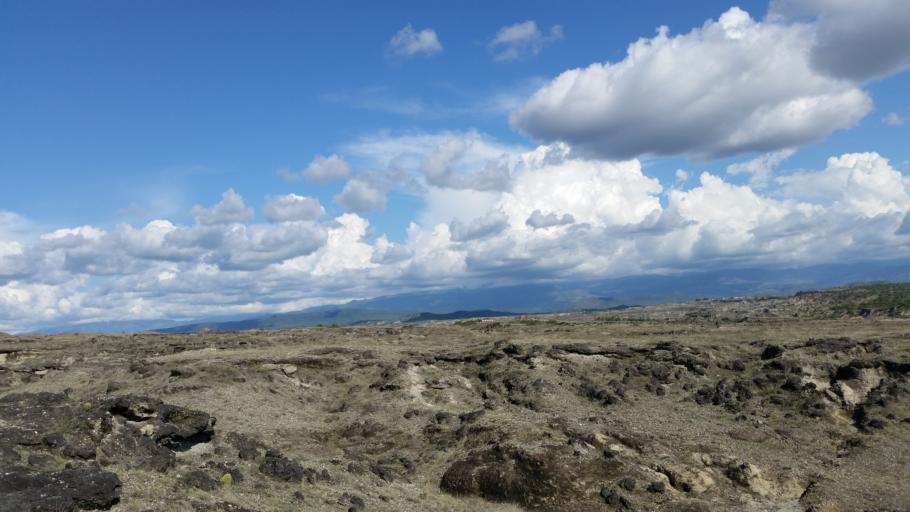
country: CO
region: Huila
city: Villavieja
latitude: 3.2535
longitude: -75.1439
